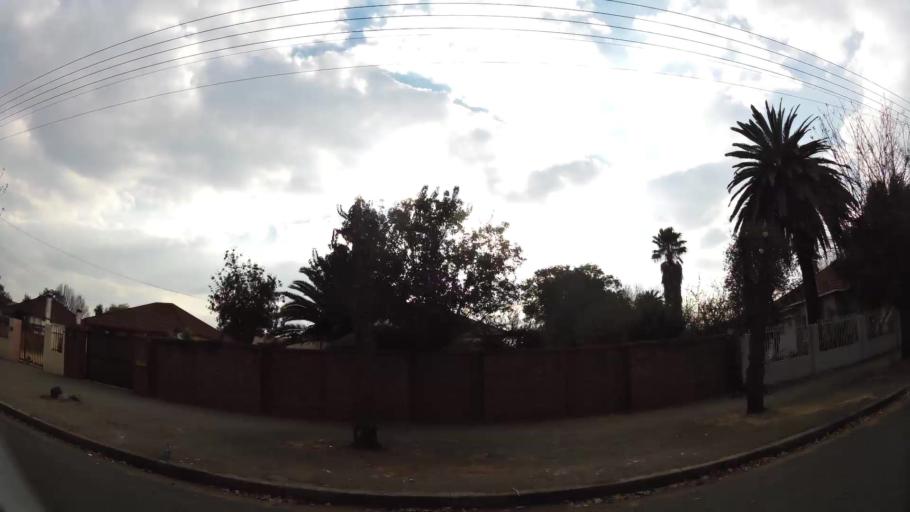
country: ZA
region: Gauteng
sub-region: Ekurhuleni Metropolitan Municipality
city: Germiston
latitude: -26.2278
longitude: 28.1682
